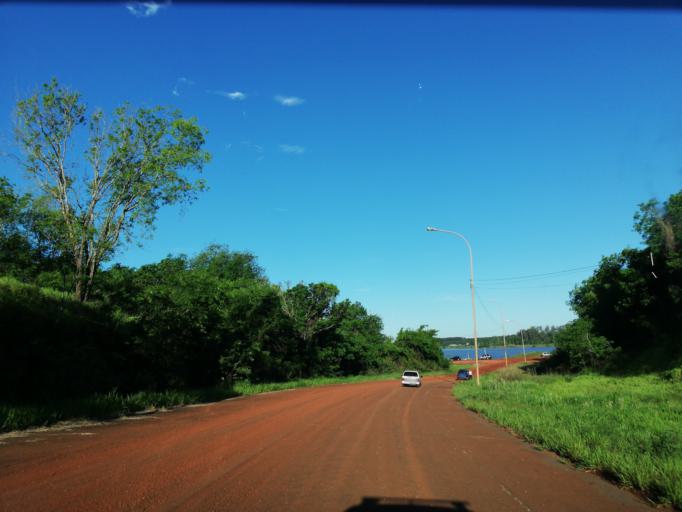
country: AR
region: Misiones
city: Garupa
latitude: -27.4581
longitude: -55.8144
